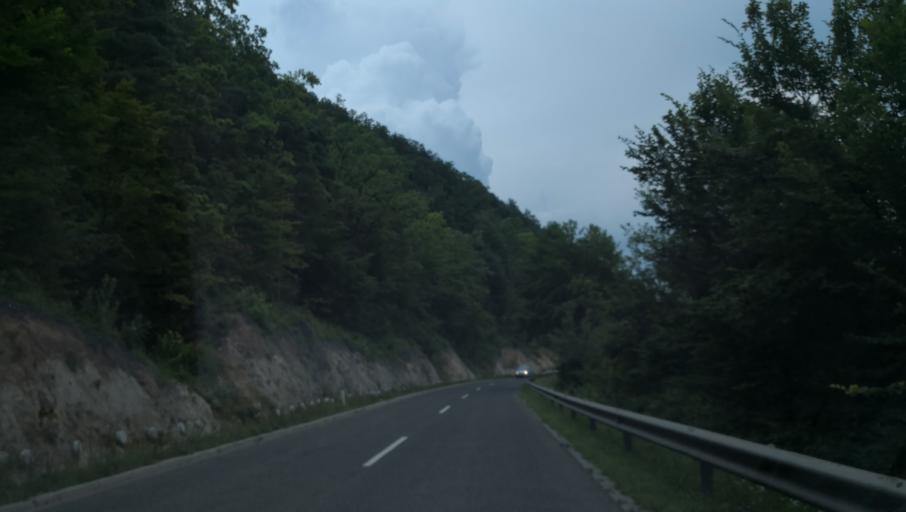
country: SI
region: Zuzemberk
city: Zuzemberk
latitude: 45.8274
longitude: 14.9474
